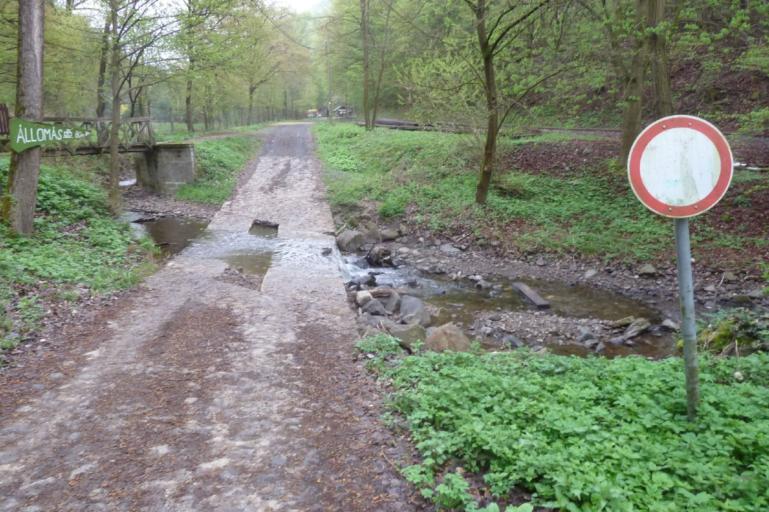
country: HU
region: Pest
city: Szob
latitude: 47.9311
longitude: 18.8392
